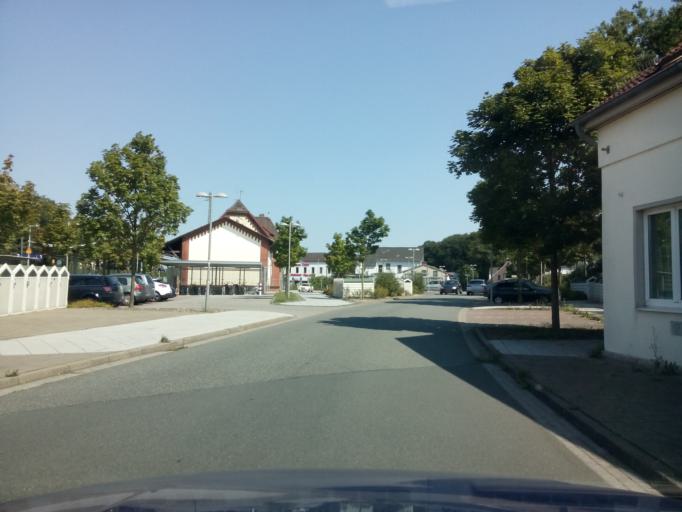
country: DE
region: Lower Saxony
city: Osterholz-Scharmbeck
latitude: 53.2220
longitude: 8.7973
